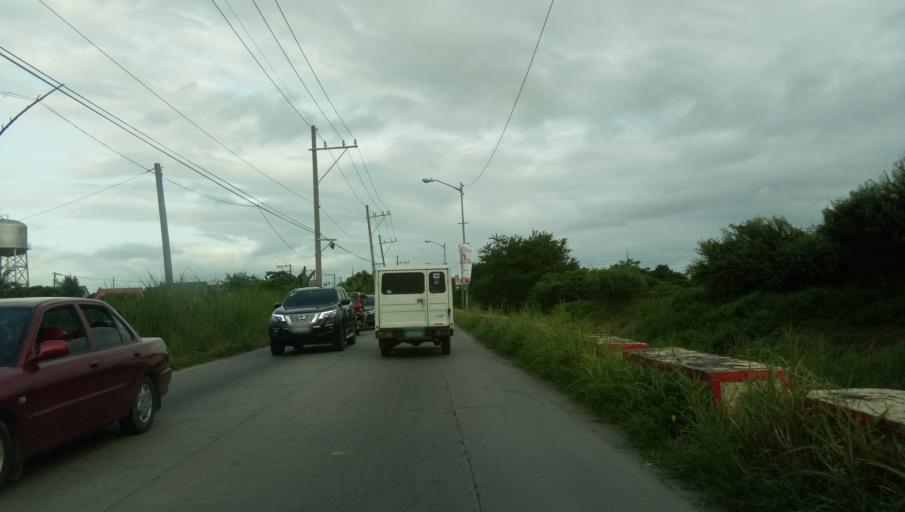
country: PH
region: Calabarzon
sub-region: Province of Cavite
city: Dasmarinas
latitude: 14.3675
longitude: 120.9305
